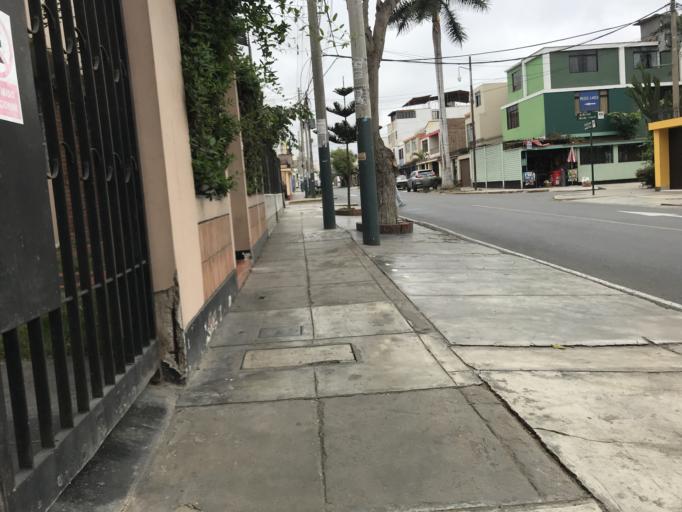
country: PE
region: Lima
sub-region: Lima
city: San Isidro
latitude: -12.0744
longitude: -77.0718
